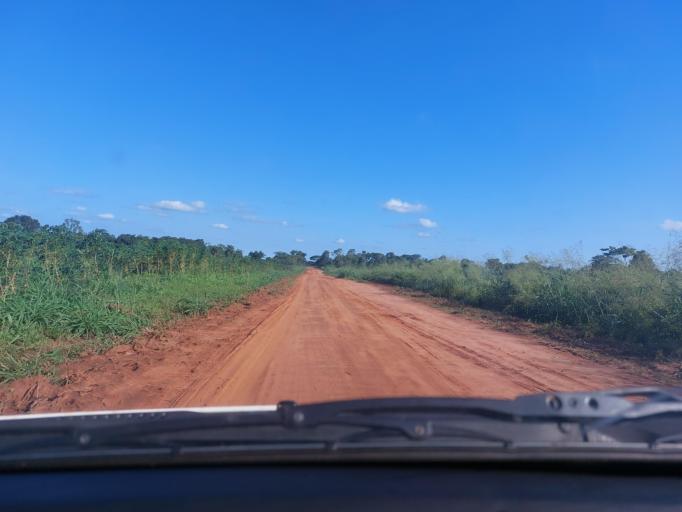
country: PY
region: San Pedro
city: Guayaybi
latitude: -24.5263
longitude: -56.5454
